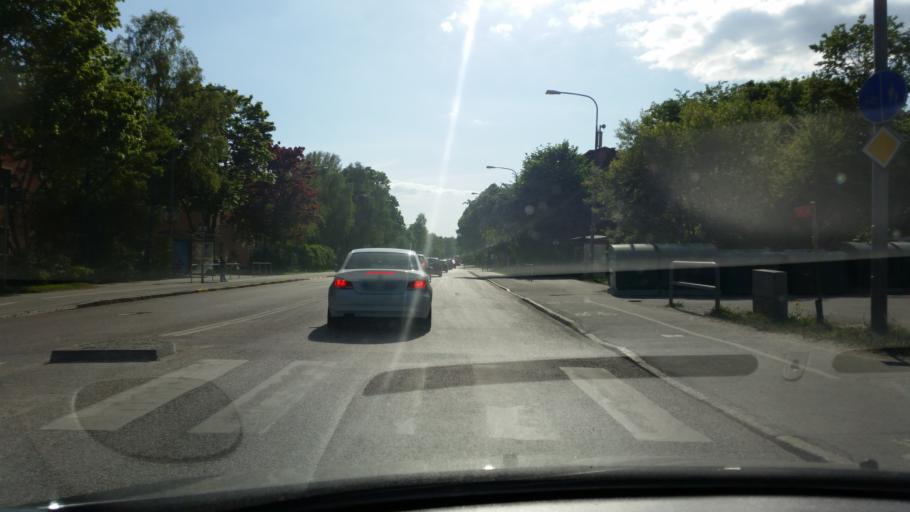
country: SE
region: Stockholm
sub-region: Stockholms Kommun
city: Bromma
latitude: 59.3424
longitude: 17.9508
